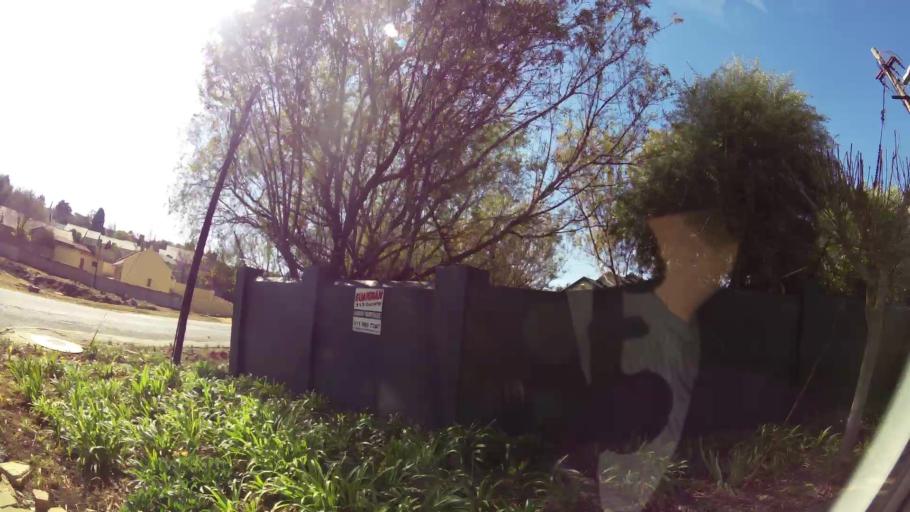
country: ZA
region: Gauteng
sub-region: City of Johannesburg Metropolitan Municipality
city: Johannesburg
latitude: -26.2779
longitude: 27.9935
